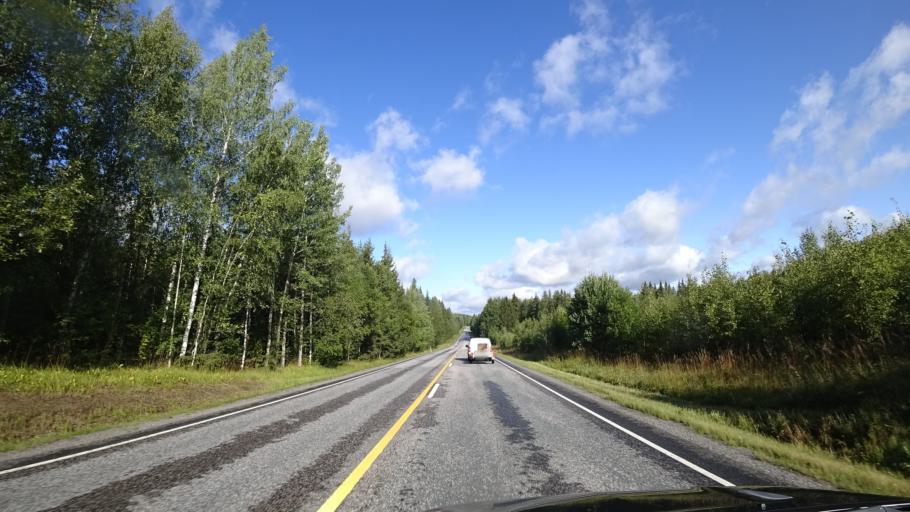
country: FI
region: Uusimaa
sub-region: Helsinki
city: Tuusula
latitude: 60.4529
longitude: 24.9560
